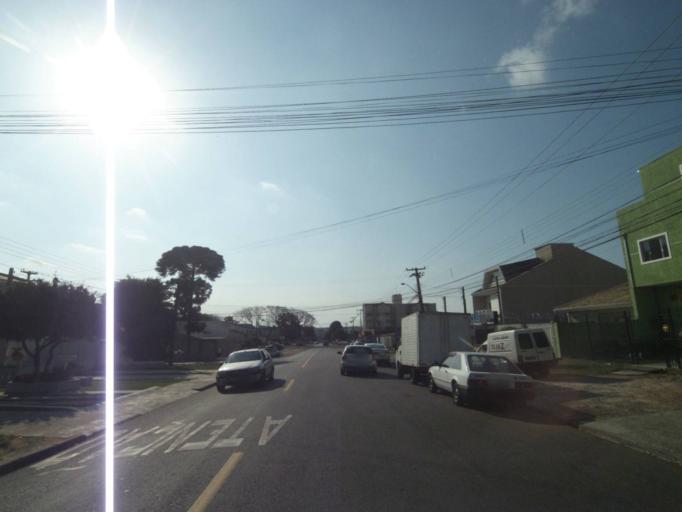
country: BR
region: Parana
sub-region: Curitiba
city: Curitiba
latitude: -25.4849
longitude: -49.3263
